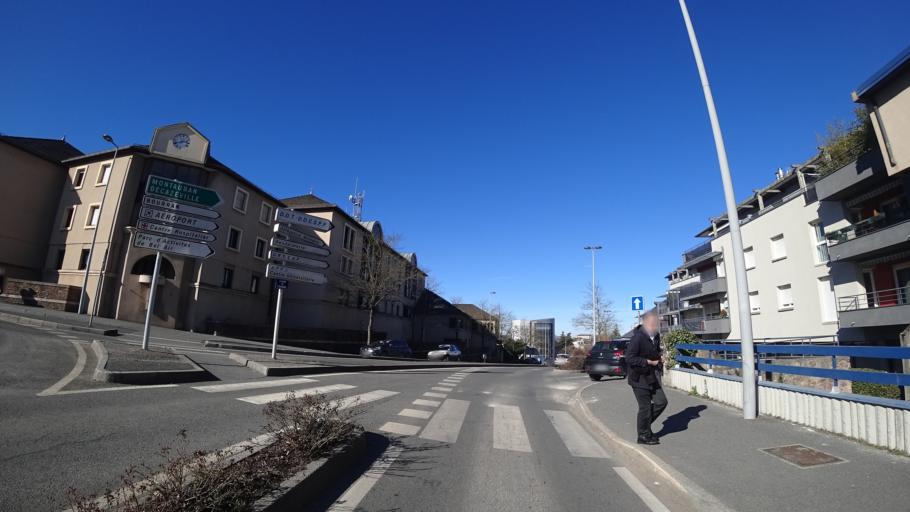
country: FR
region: Midi-Pyrenees
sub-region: Departement de l'Aveyron
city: Rodez
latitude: 44.3530
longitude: 2.5661
